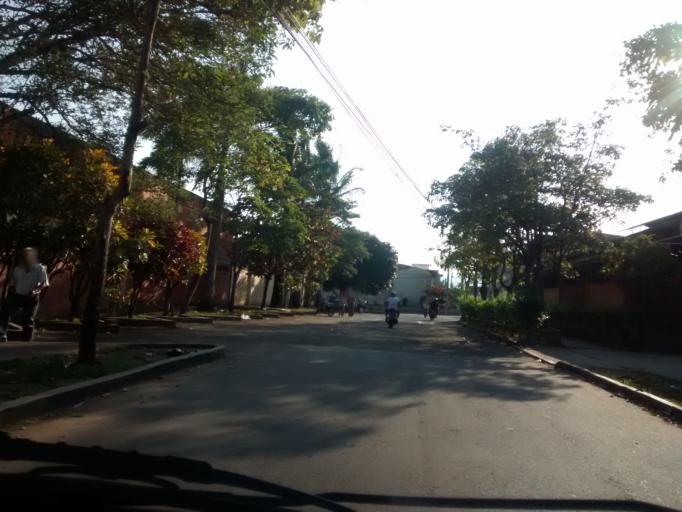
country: CO
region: Santander
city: Bucaramanga
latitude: 7.0999
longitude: -73.1299
